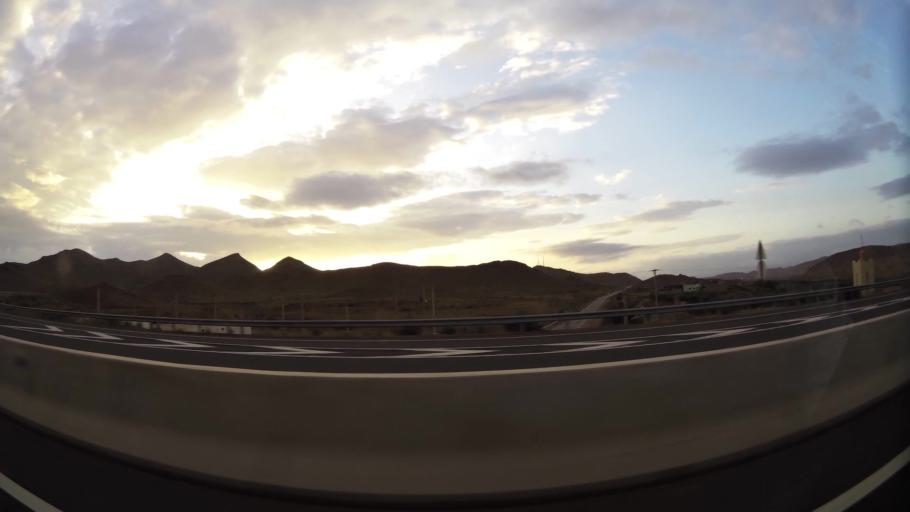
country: MA
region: Oriental
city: Taourirt
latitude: 34.4757
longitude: -2.9887
